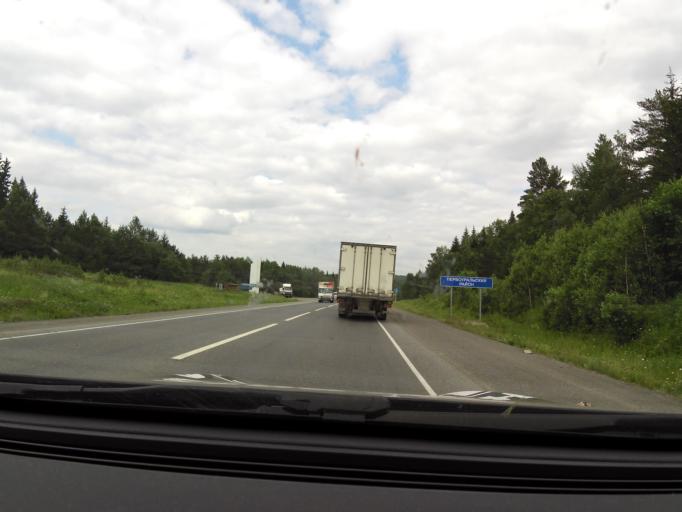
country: RU
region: Sverdlovsk
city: Druzhinino
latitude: 56.8198
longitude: 59.5676
